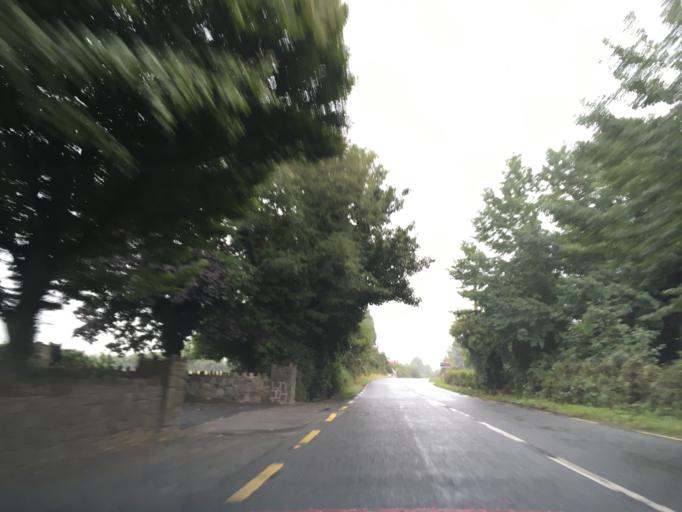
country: IE
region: Munster
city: Tipperary
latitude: 52.4801
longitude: -8.1175
